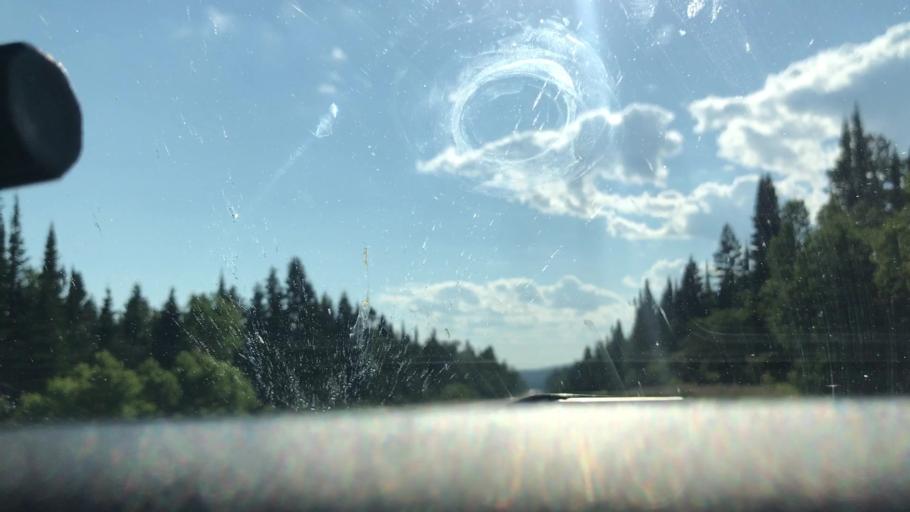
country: US
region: Minnesota
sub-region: Cook County
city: Grand Marais
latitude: 47.7963
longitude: -90.1275
